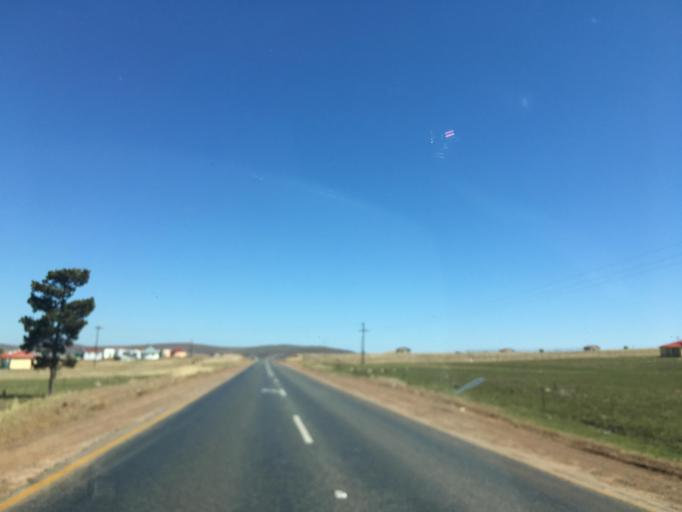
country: ZA
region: Eastern Cape
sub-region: Chris Hani District Municipality
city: Cofimvaba
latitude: -31.9561
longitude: 27.8263
